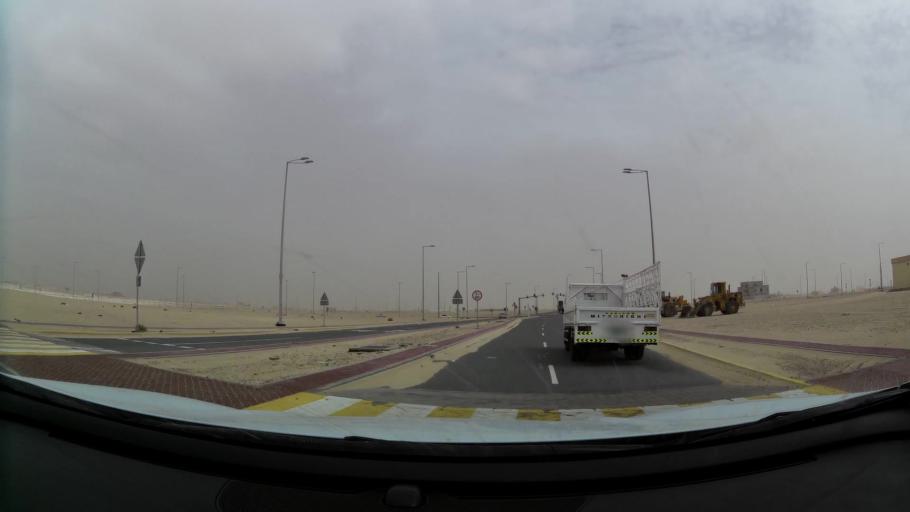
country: AE
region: Abu Dhabi
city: Abu Dhabi
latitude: 24.3697
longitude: 54.7456
